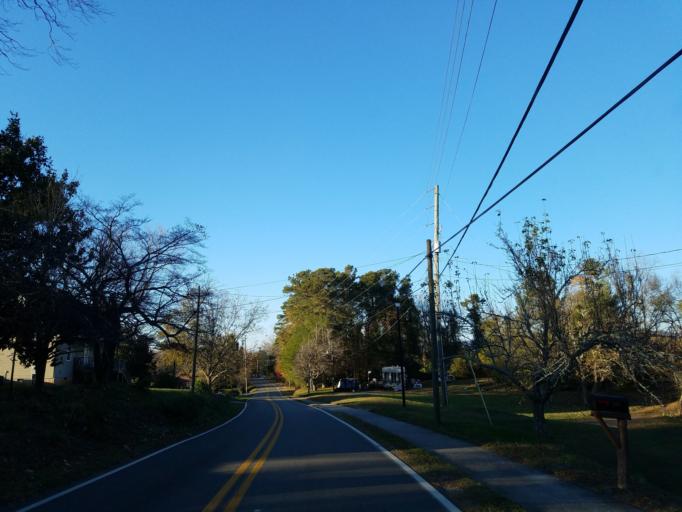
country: US
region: Georgia
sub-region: Pickens County
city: Nelson
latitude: 34.3811
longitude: -84.3659
